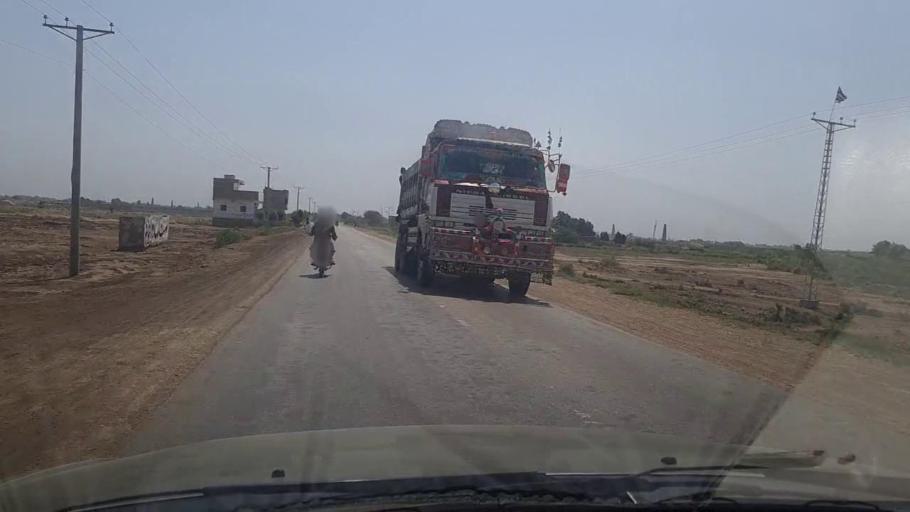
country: PK
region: Sindh
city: Hyderabad
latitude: 25.3838
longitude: 68.4394
